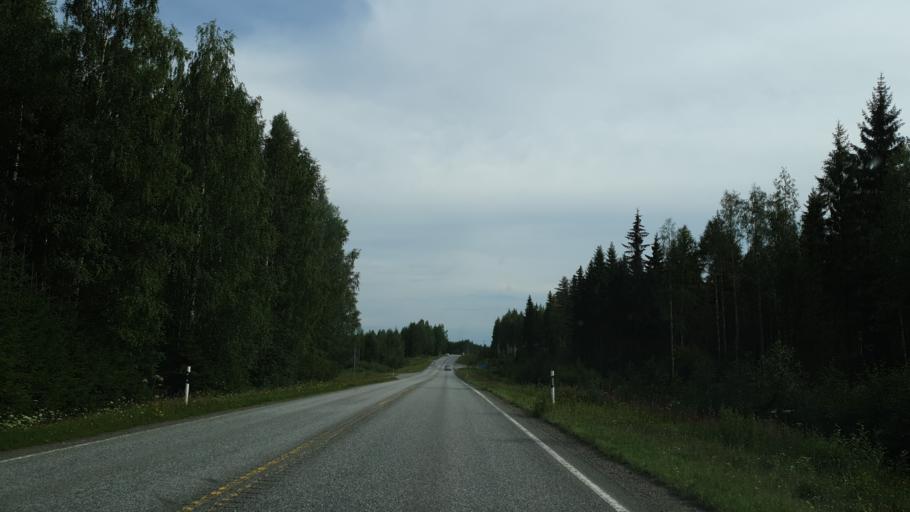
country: FI
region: North Karelia
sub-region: Joensuu
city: Kontiolahti
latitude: 62.7938
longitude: 29.8480
